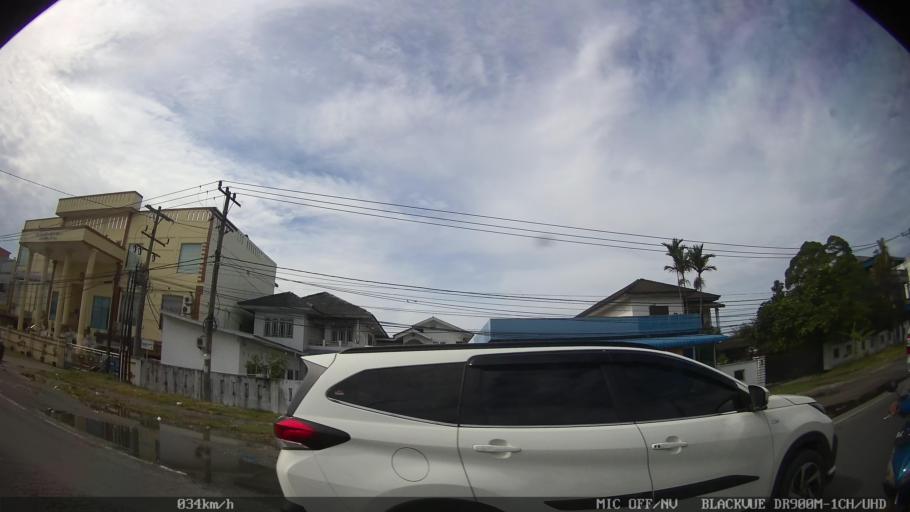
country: ID
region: North Sumatra
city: Medan
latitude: 3.6148
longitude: 98.6464
